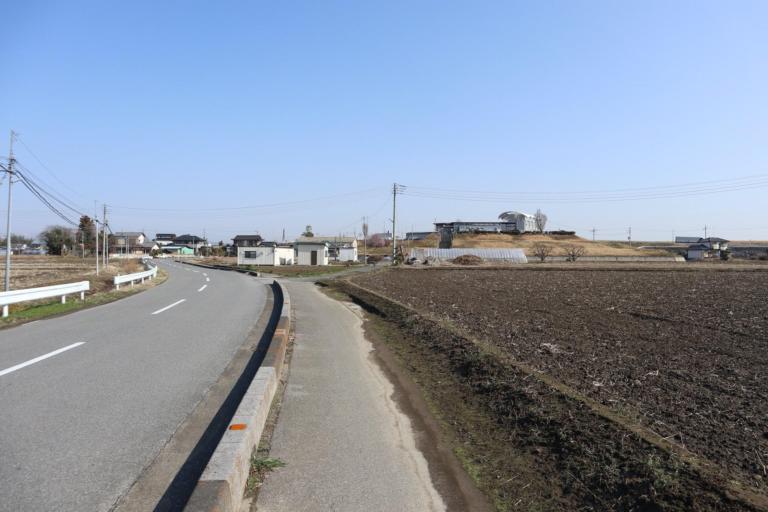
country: JP
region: Tochigi
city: Fujioka
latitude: 36.2091
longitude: 139.6610
